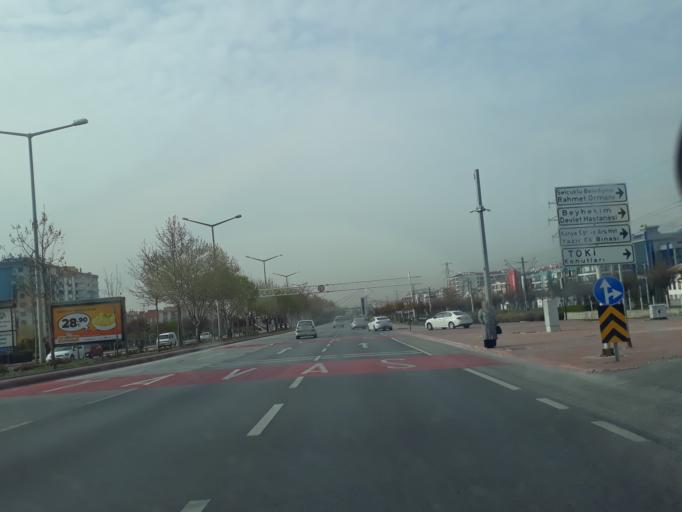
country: TR
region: Konya
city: Selcuklu
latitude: 37.9795
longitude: 32.5167
